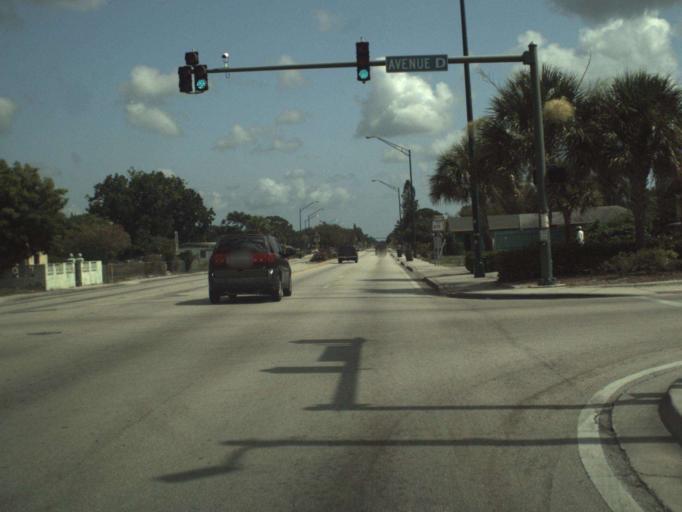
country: US
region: Florida
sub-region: Saint Lucie County
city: Fort Pierce North
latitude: 27.4528
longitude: -80.3498
